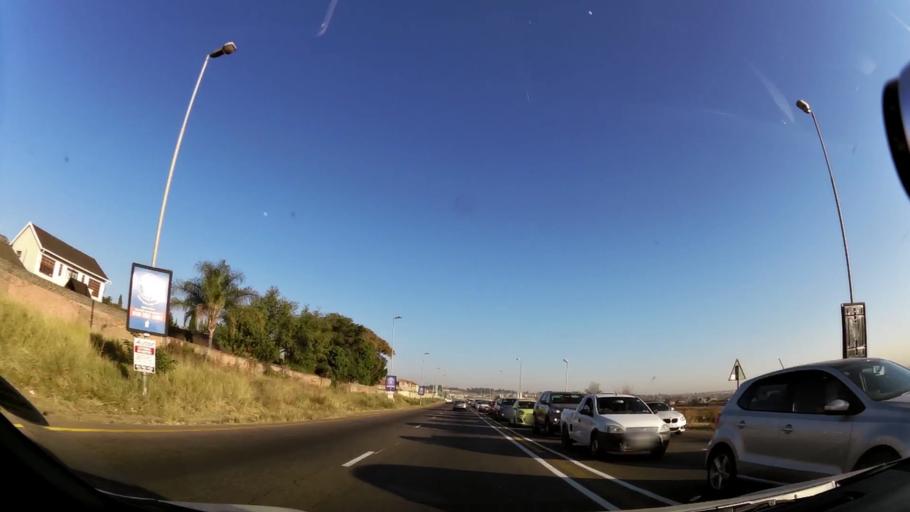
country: ZA
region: Gauteng
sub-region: City of Johannesburg Metropolitan Municipality
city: Midrand
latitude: -25.9497
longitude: 28.1211
